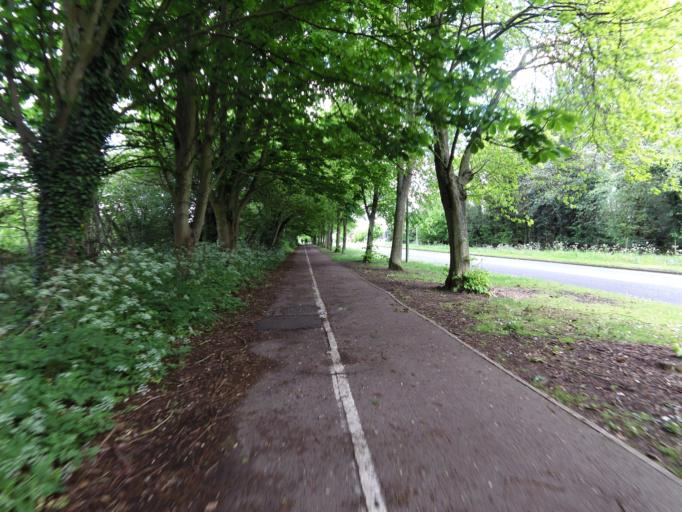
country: GB
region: England
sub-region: Suffolk
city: Bury St Edmunds
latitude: 52.2441
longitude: 0.7380
